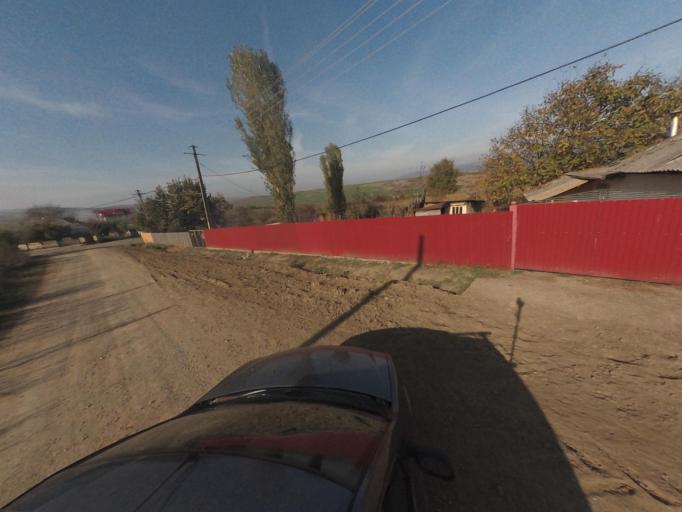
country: RO
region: Vaslui
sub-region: Comuna Bacesti
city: Bacesti
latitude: 46.8703
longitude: 27.2053
